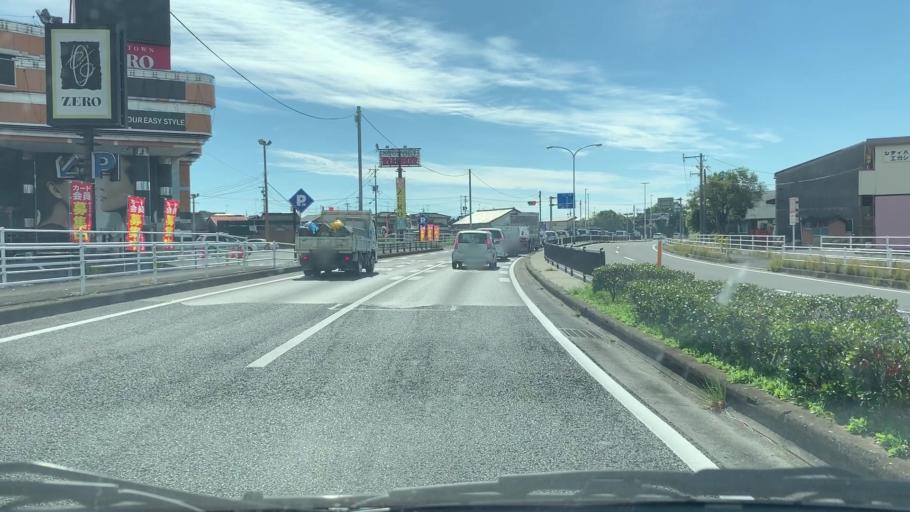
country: JP
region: Saga Prefecture
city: Saga-shi
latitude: 33.2499
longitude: 130.1986
